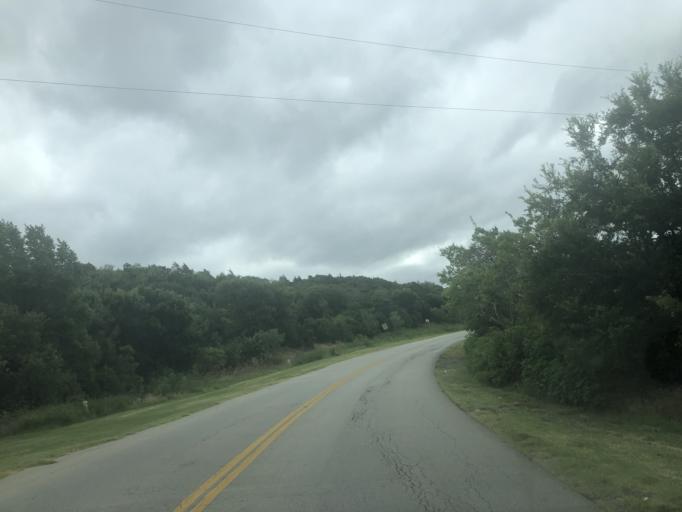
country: US
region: Texas
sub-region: Dallas County
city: Duncanville
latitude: 32.6655
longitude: -96.9588
